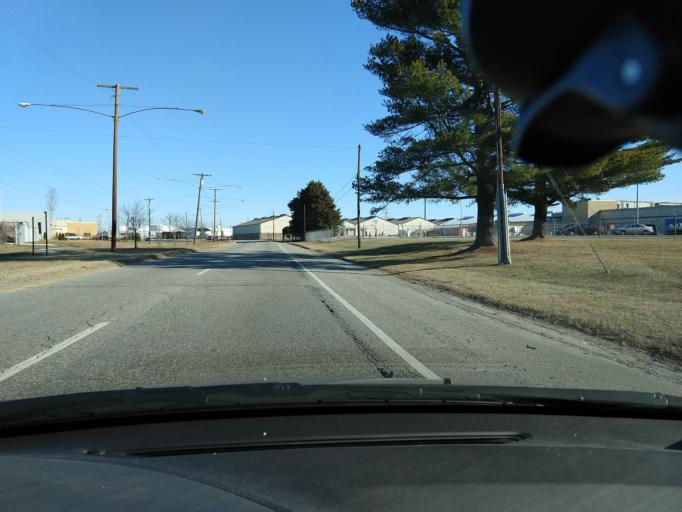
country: US
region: Virginia
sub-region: Chesterfield County
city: Bensley
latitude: 37.4986
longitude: -77.4321
